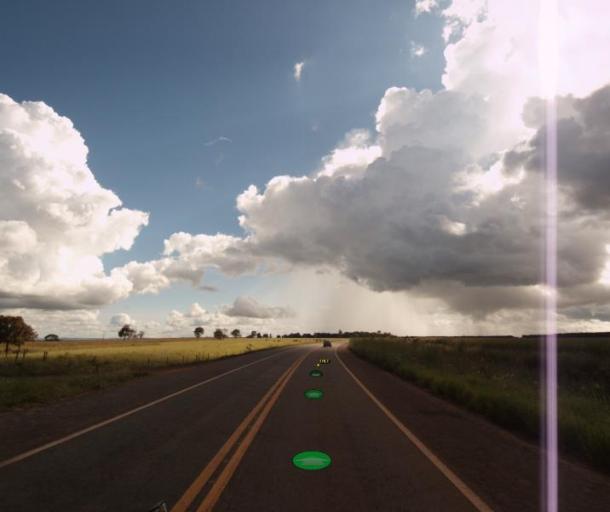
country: BR
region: Goias
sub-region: Itaberai
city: Itaberai
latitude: -15.9849
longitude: -49.6945
